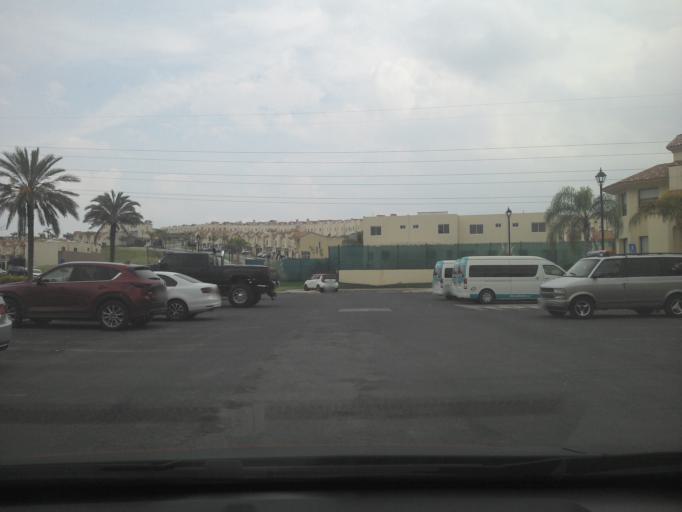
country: MX
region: Jalisco
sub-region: Tlajomulco de Zuniga
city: Lomas de San Agustin
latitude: 20.5289
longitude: -103.4627
